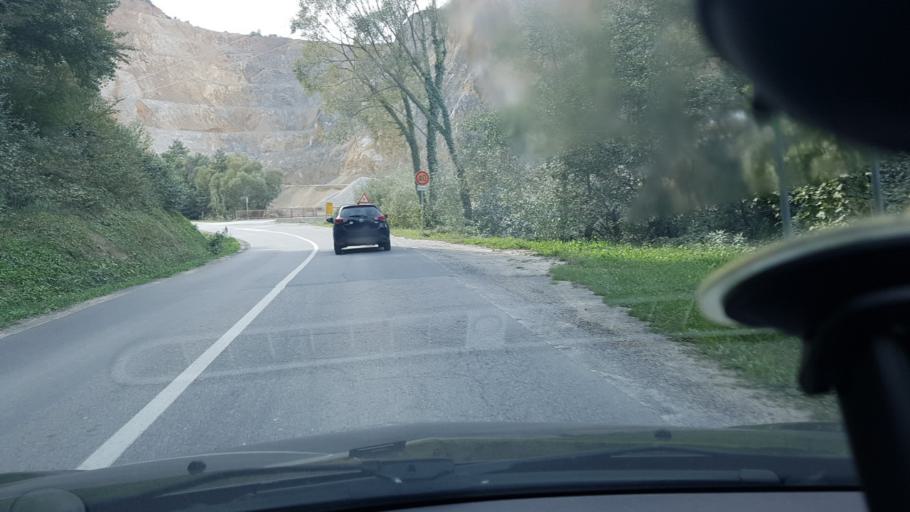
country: HR
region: Varazdinska
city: Lepoglava
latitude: 46.1916
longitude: 15.9881
